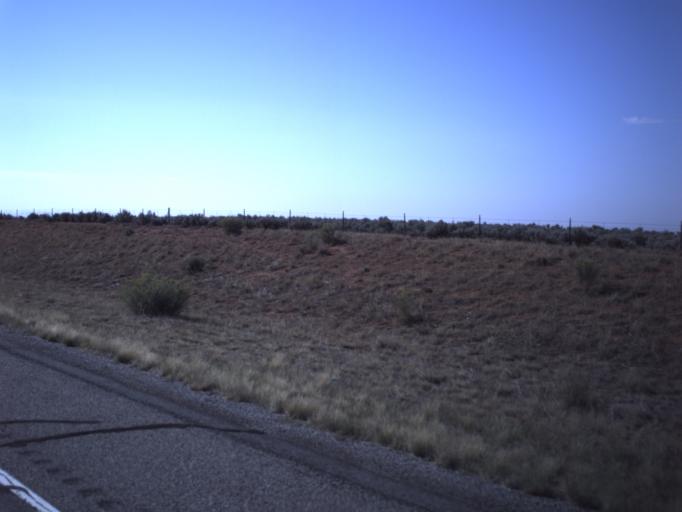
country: US
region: Utah
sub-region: San Juan County
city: Blanding
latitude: 37.4983
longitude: -109.4841
